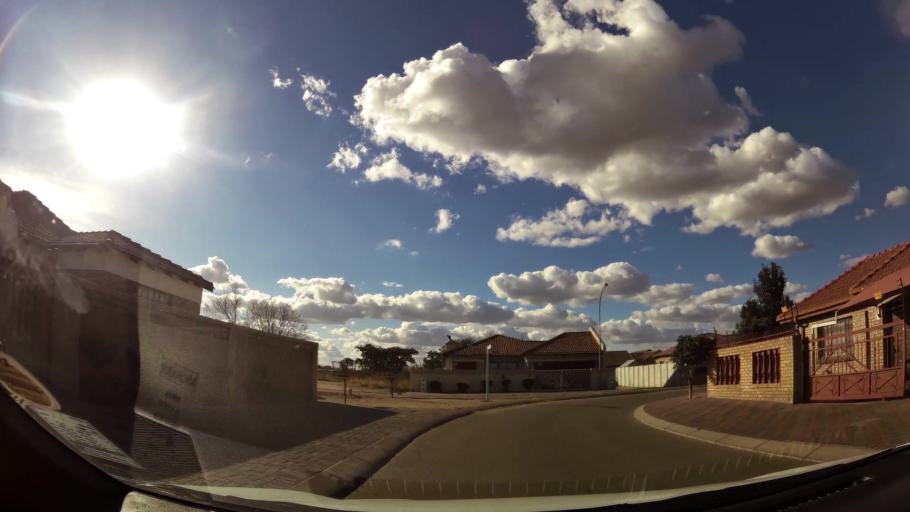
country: ZA
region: Limpopo
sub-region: Capricorn District Municipality
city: Polokwane
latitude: -23.9383
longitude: 29.4426
